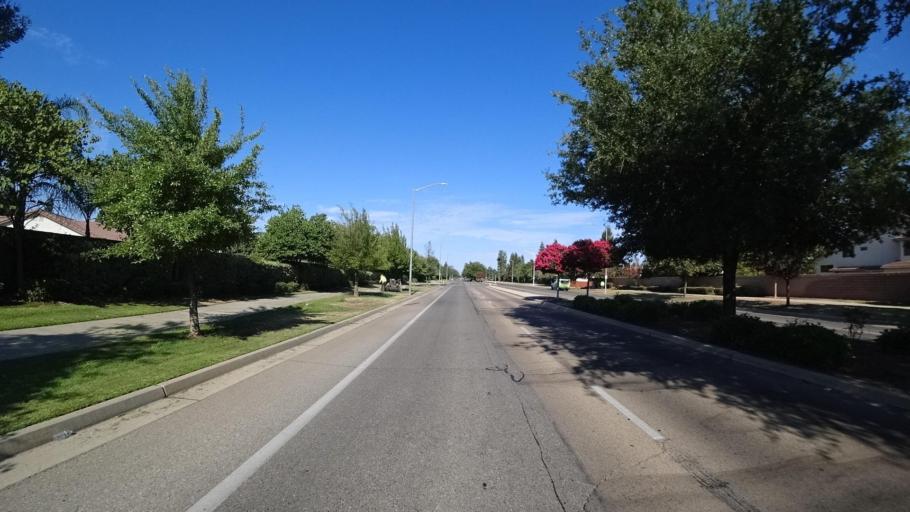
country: US
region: California
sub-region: Fresno County
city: Tarpey Village
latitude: 36.7938
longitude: -119.6586
